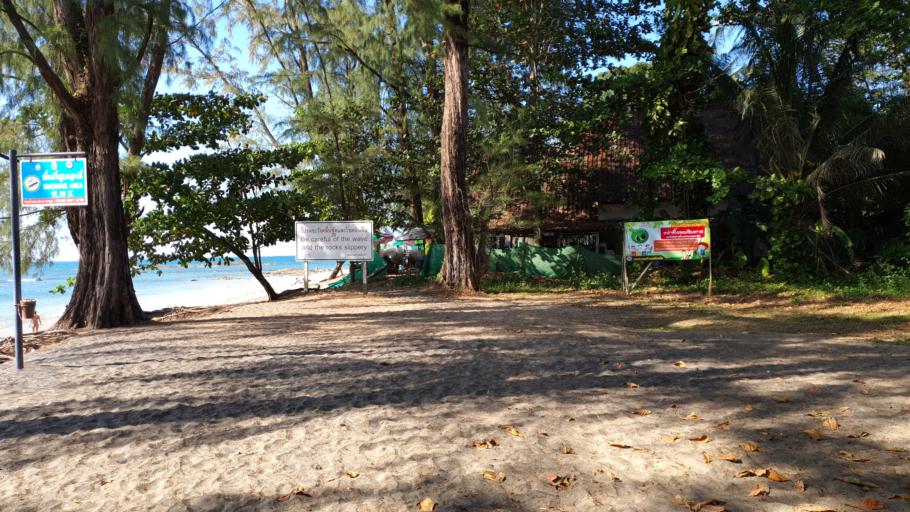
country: TH
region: Phangnga
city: Ban Khao Lak
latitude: 8.6455
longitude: 98.2464
